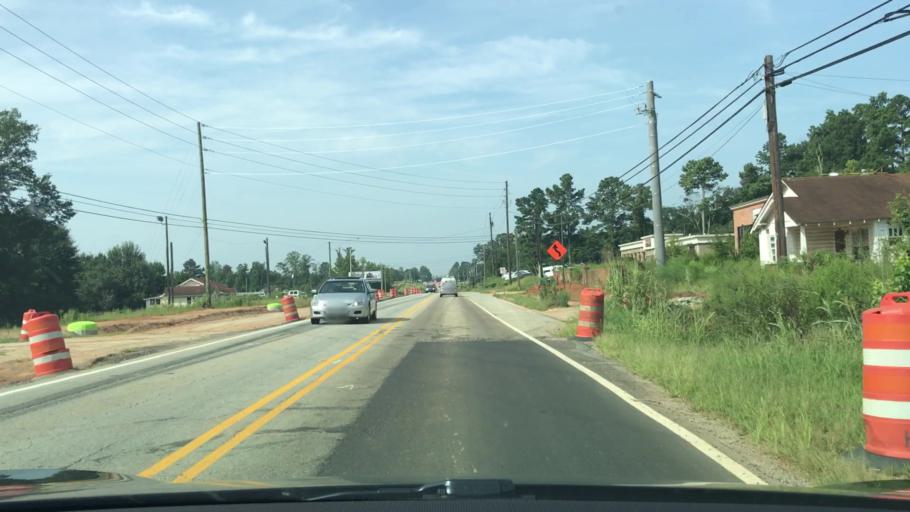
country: US
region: Georgia
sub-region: Gwinnett County
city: Buford
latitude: 34.1328
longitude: -83.9772
